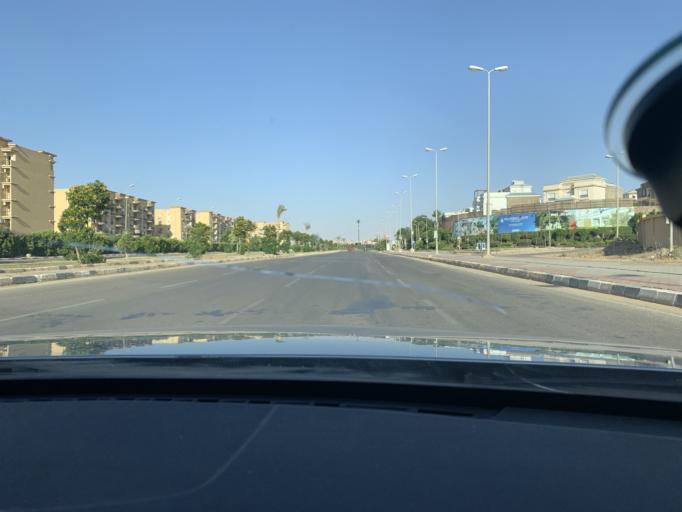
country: EG
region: Muhafazat al Qalyubiyah
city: Al Khankah
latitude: 30.0527
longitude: 31.5047
